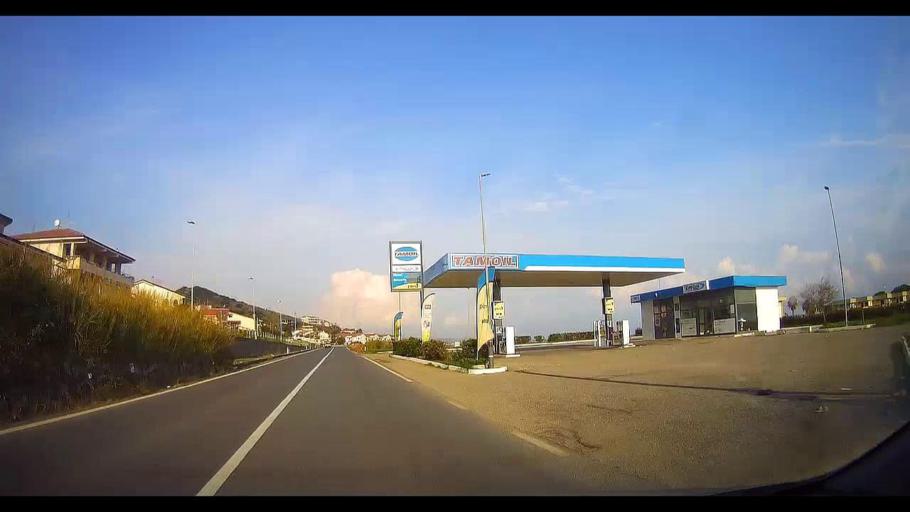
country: IT
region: Calabria
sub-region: Provincia di Cosenza
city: Cariati
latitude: 39.5253
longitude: 16.8916
